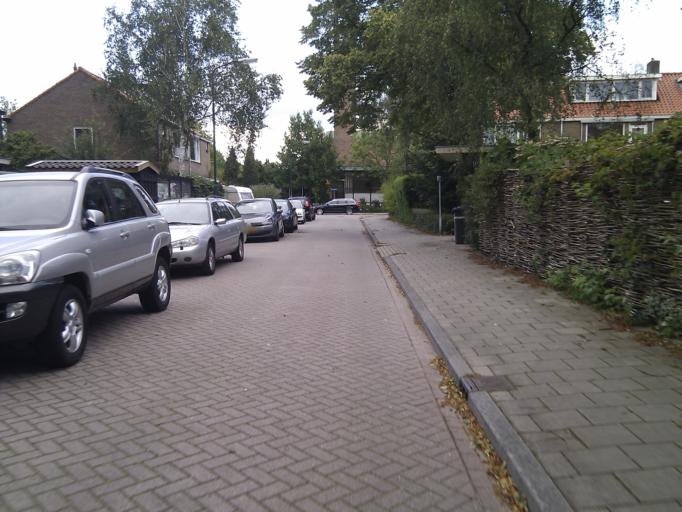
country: NL
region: Utrecht
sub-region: Gemeente De Bilt
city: De Bilt
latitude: 52.1155
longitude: 5.1846
